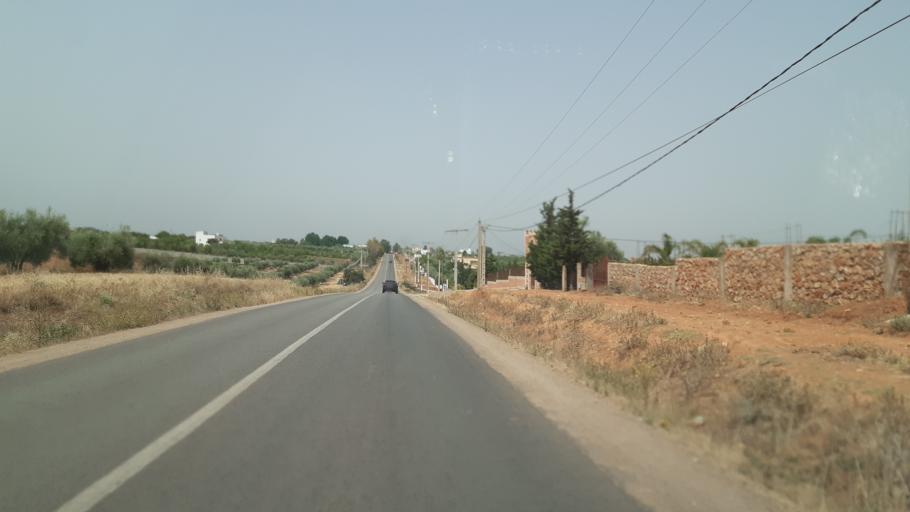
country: MA
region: Fes-Boulemane
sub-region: Fes
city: Oulad Tayeb
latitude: 33.8951
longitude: -5.0228
